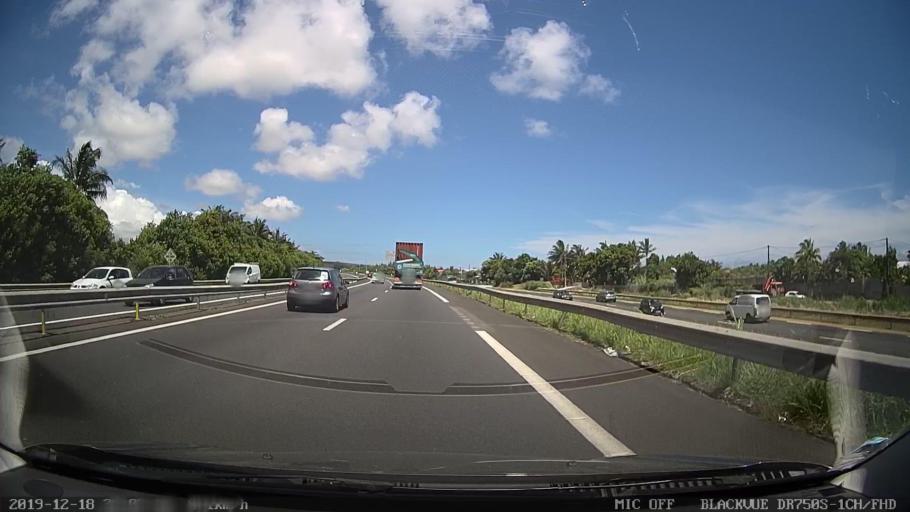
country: RE
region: Reunion
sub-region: Reunion
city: Sainte-Suzanne
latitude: -20.9171
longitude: 55.6239
